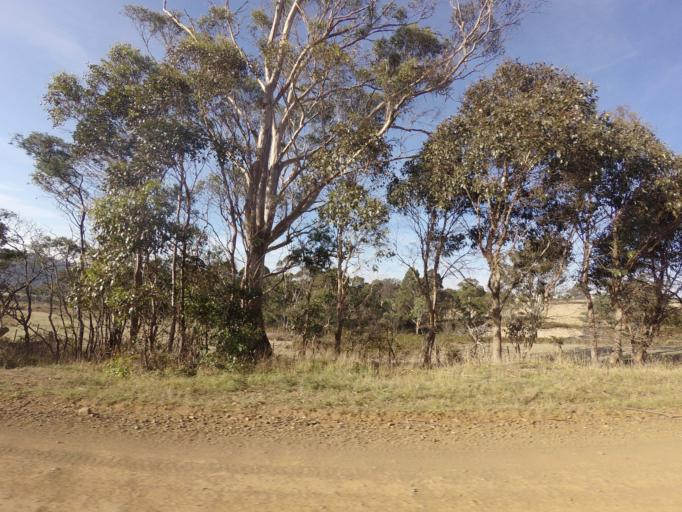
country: AU
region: Tasmania
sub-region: Brighton
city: Bridgewater
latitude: -42.4834
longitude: 147.3861
